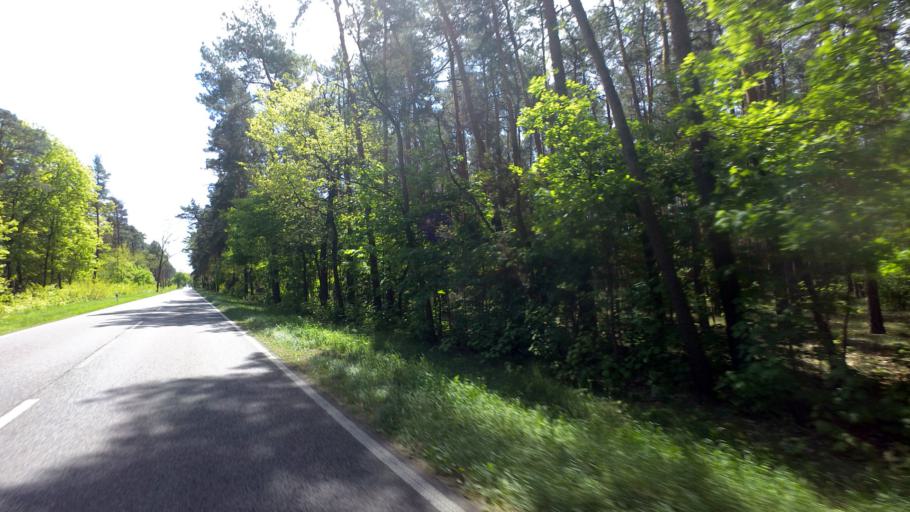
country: DE
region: Brandenburg
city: Luckenwalde
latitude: 52.1553
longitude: 13.1047
